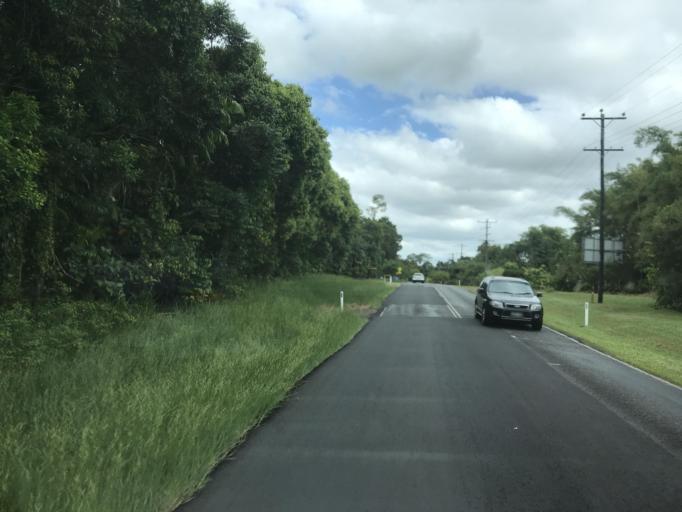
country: AU
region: Queensland
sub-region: Cassowary Coast
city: Innisfail
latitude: -17.8280
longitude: 146.0553
